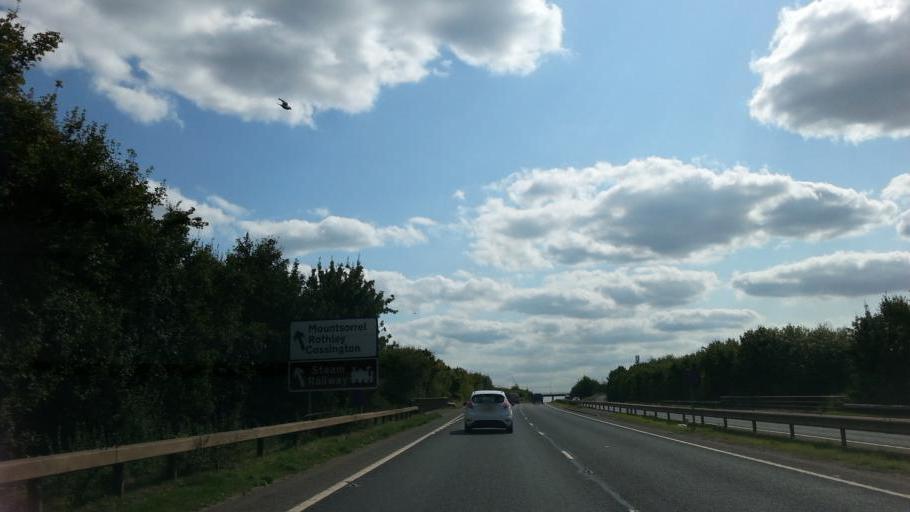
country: GB
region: England
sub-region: Leicestershire
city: Mountsorrel
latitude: 52.7242
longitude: -1.1287
